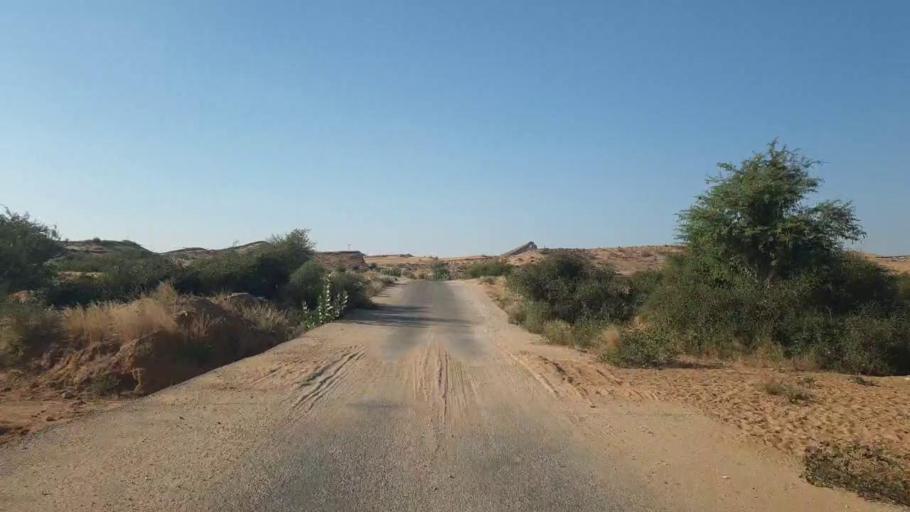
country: PK
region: Sindh
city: Malir Cantonment
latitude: 25.4005
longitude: 67.4900
